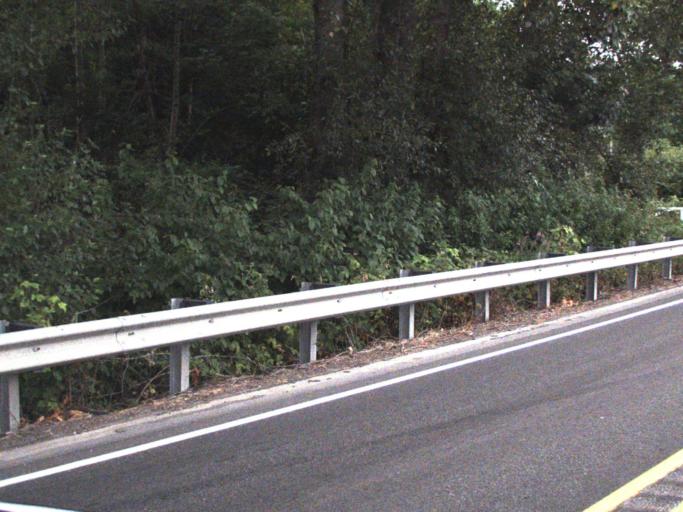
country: US
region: Washington
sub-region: King County
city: Fall City
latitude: 47.5953
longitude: -121.9119
